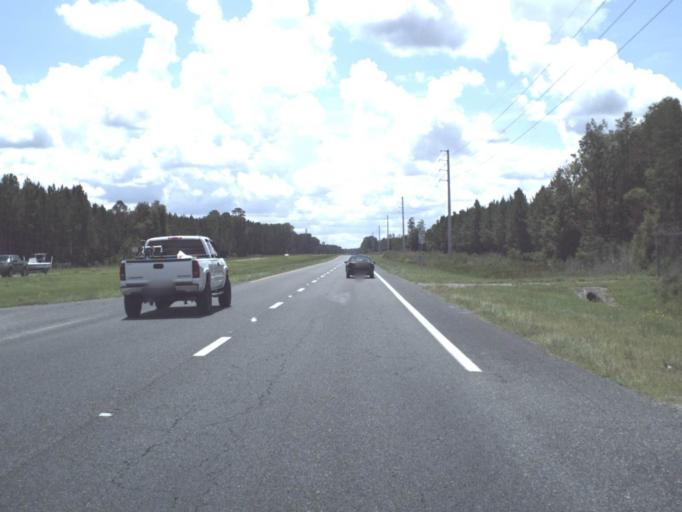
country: US
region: Florida
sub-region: Levy County
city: Bronson
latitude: 29.4687
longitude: -82.6722
